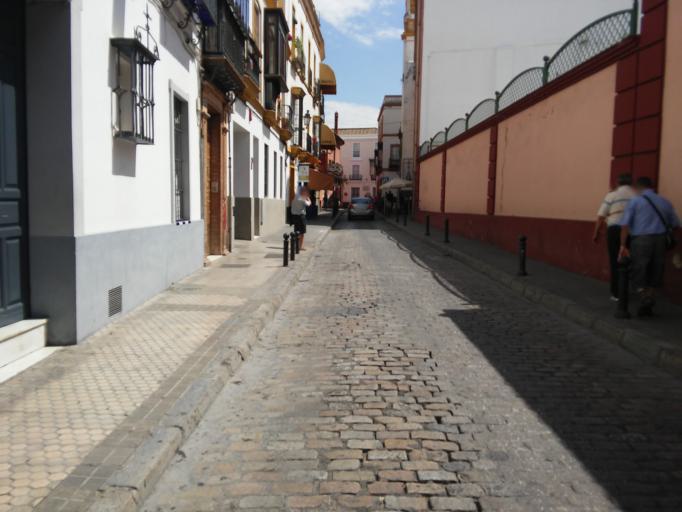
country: ES
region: Andalusia
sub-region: Provincia de Sevilla
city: Sevilla
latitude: 37.3861
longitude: -5.9901
